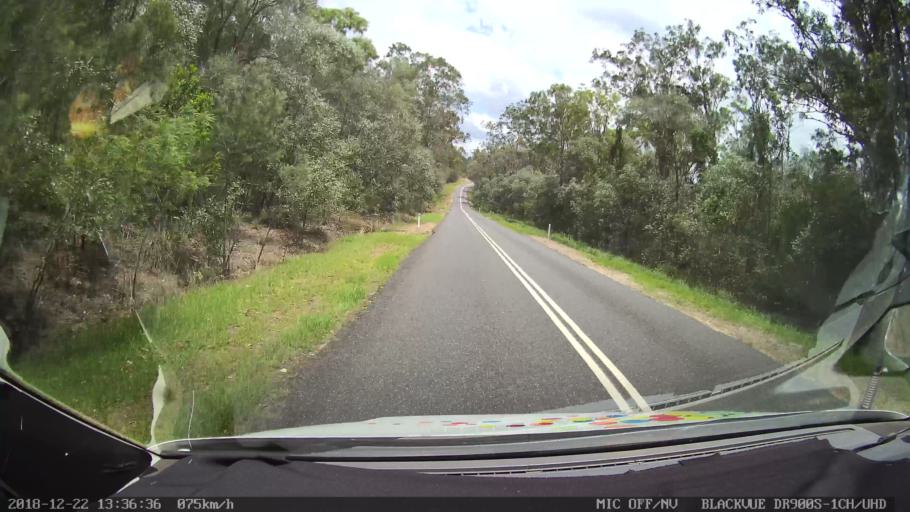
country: AU
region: New South Wales
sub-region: Clarence Valley
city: Coutts Crossing
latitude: -29.8811
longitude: 152.7933
